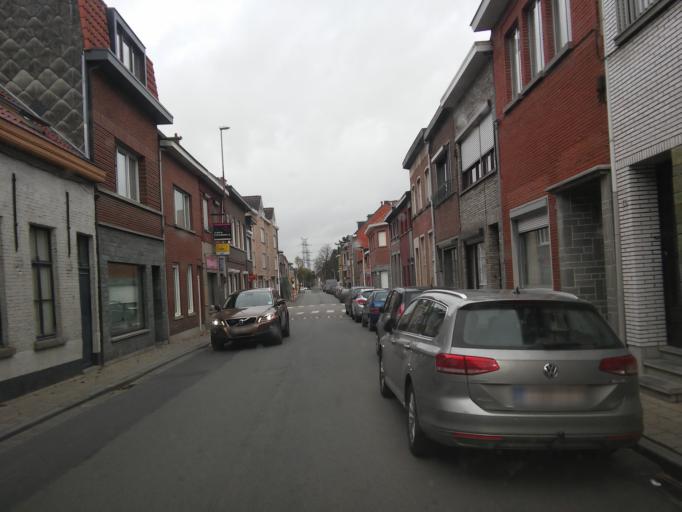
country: BE
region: Flanders
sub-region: Provincie Antwerpen
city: Niel
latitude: 51.1293
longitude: 4.2924
